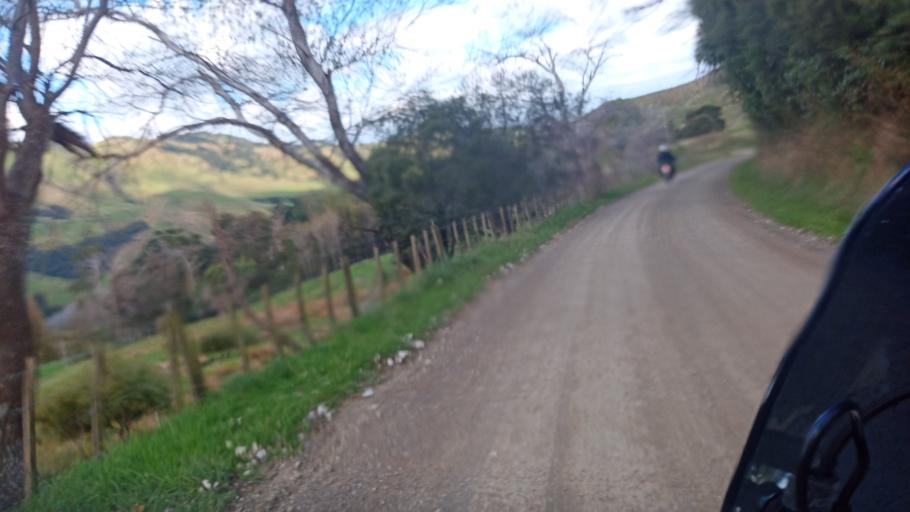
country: NZ
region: Gisborne
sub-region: Gisborne District
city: Gisborne
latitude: -38.4597
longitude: 177.6340
